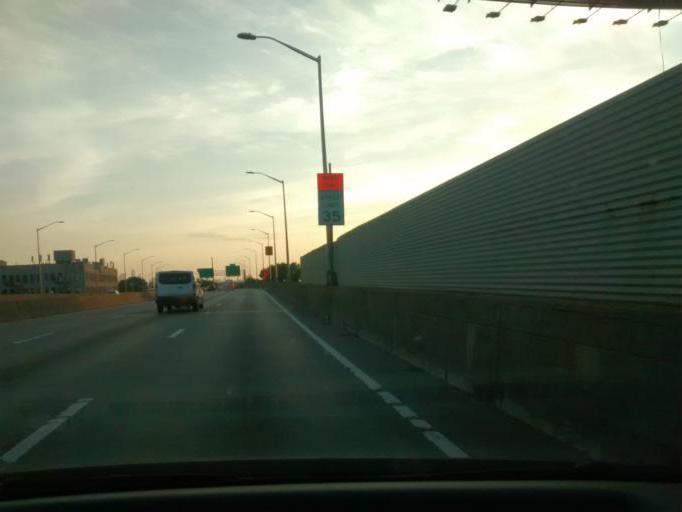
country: US
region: New York
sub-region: Queens County
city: Long Island City
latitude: 40.7355
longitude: -73.9170
